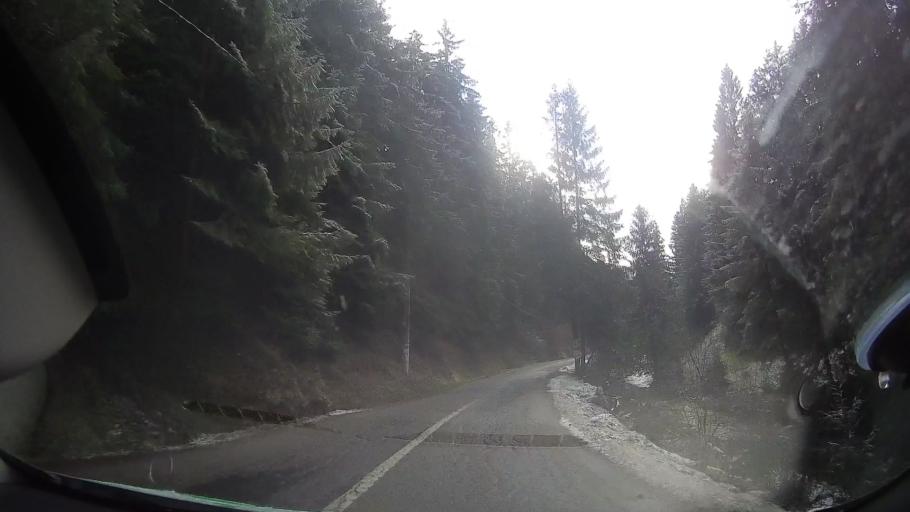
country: RO
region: Alba
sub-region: Comuna Horea
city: Horea
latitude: 46.4931
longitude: 22.9616
